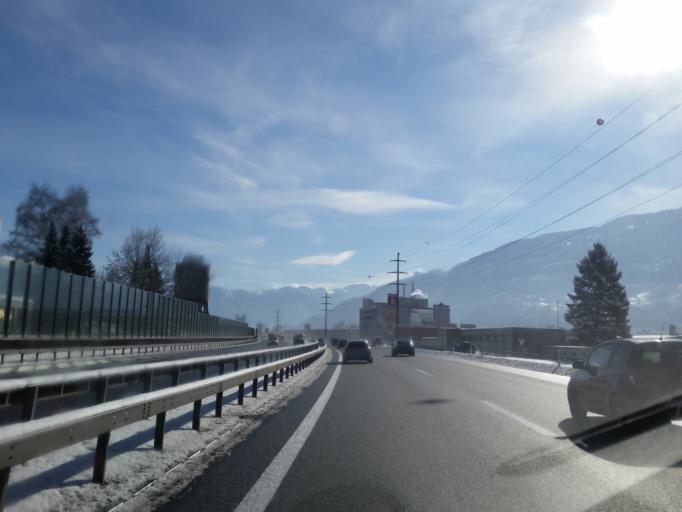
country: CH
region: Saint Gallen
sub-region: Wahlkreis Sarganserland
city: Sargans
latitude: 47.0426
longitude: 9.4360
